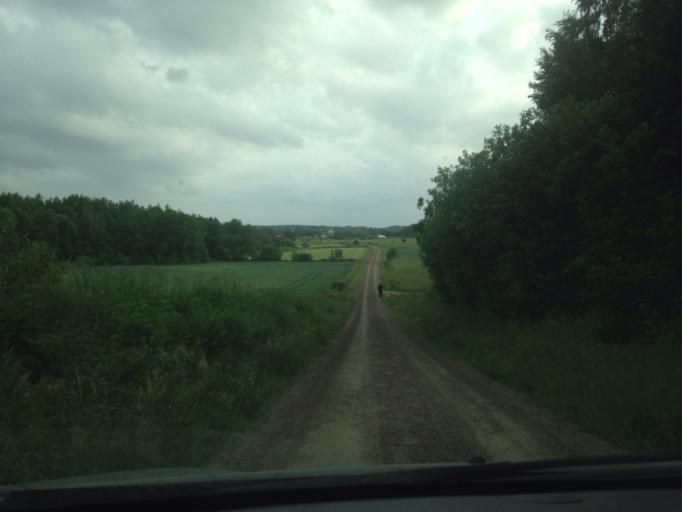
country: SE
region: Vaestra Goetaland
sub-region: Kungalvs Kommun
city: Kungalv
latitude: 57.8105
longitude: 11.9281
